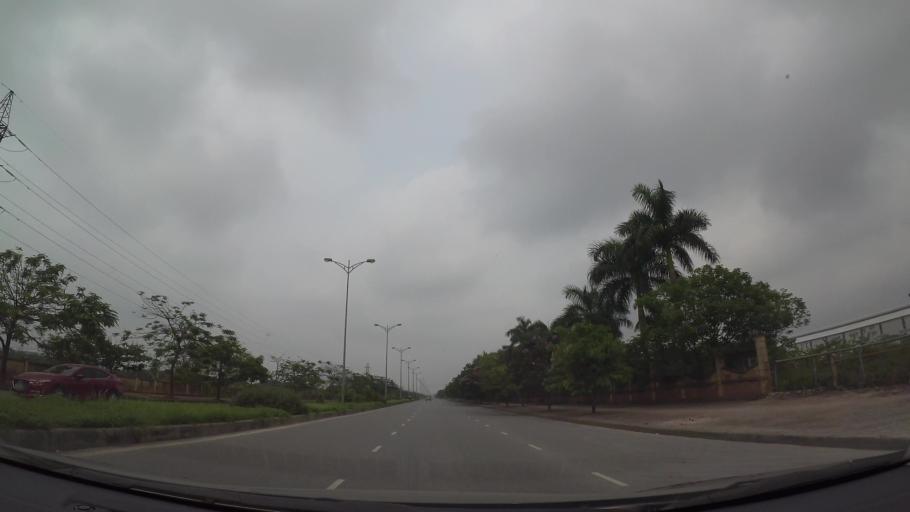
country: VN
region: Ha Noi
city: Trau Quy
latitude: 21.0315
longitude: 105.9305
